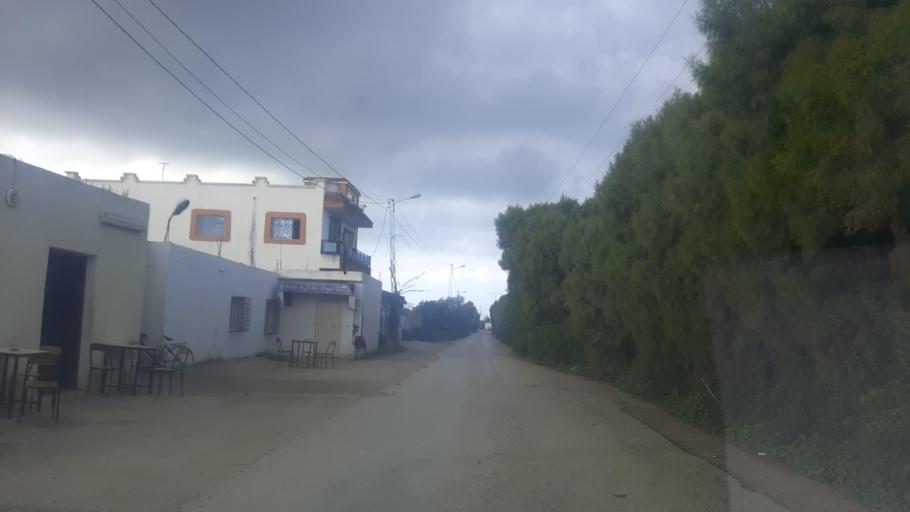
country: TN
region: Nabul
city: Manzil Bu Zalafah
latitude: 36.7335
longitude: 10.5362
